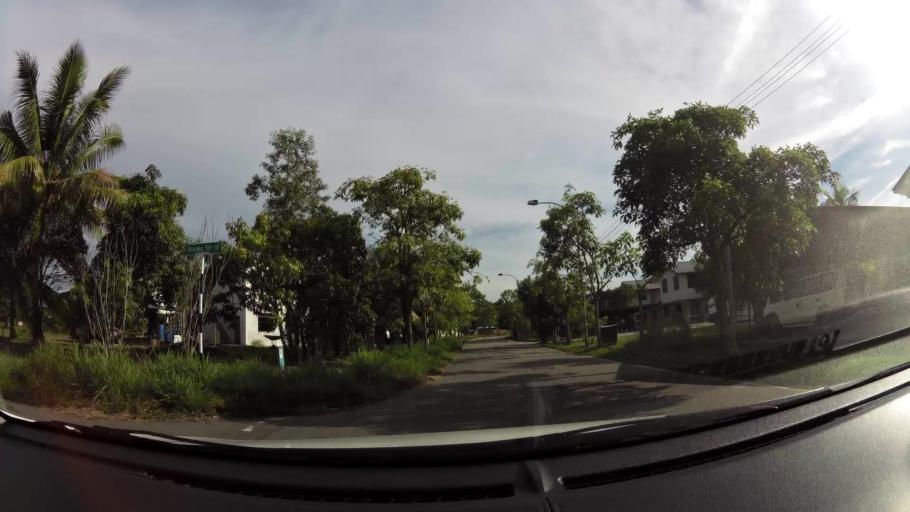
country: BN
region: Brunei and Muara
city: Bandar Seri Begawan
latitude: 4.9699
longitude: 115.0266
